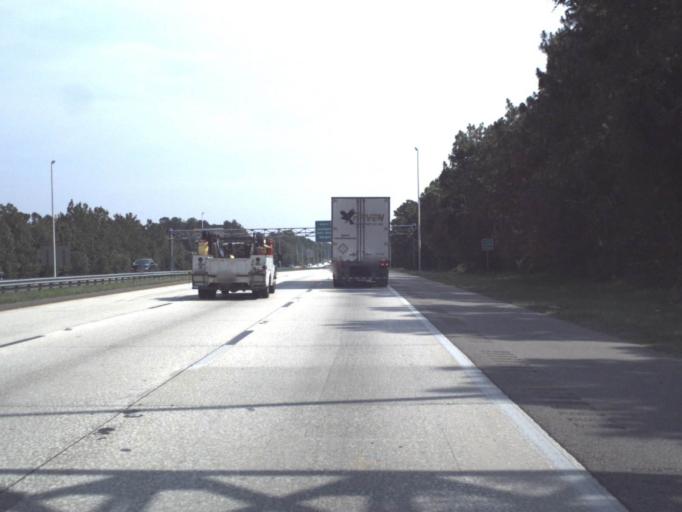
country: US
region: Florida
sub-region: Duval County
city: Jacksonville
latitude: 30.4419
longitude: -81.6543
